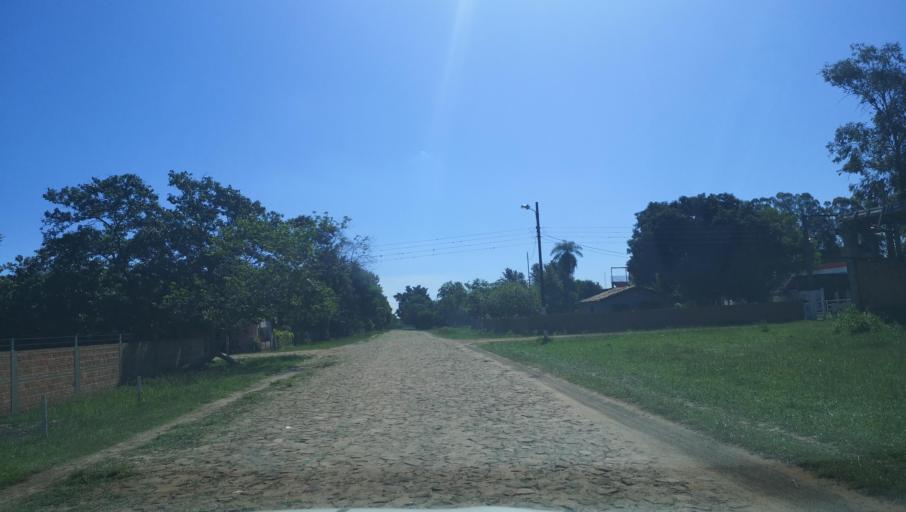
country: PY
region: Caaguazu
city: Carayao
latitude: -25.1949
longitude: -56.4004
